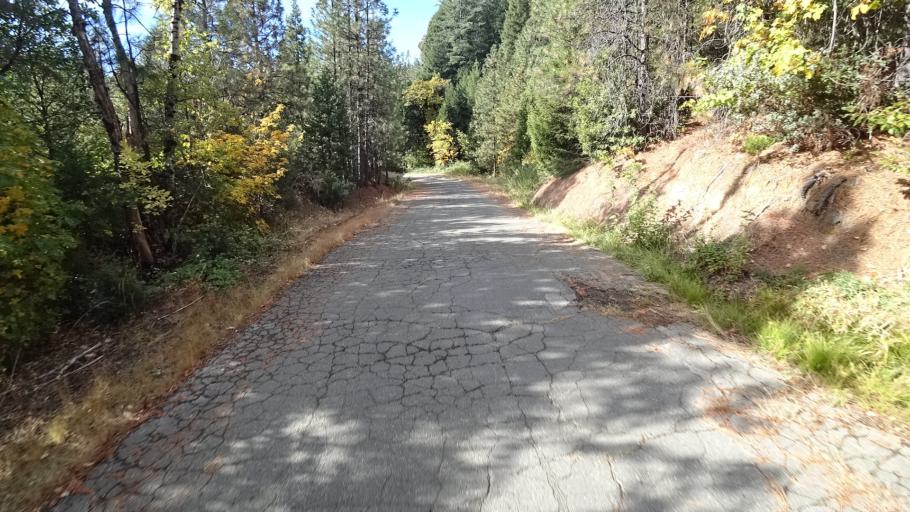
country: US
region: California
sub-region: Siskiyou County
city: Dunsmuir
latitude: 41.1033
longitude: -122.3389
